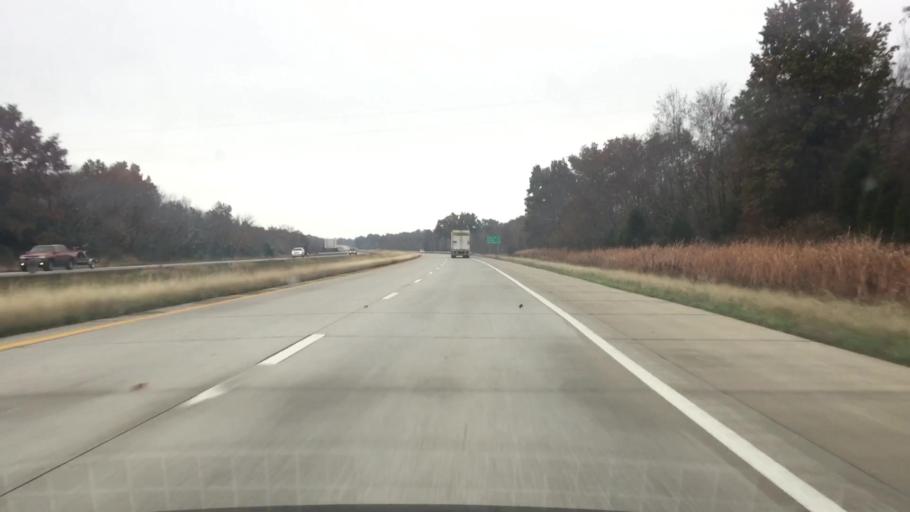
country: US
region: Missouri
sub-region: Henry County
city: Clinton
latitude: 38.2341
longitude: -93.7631
